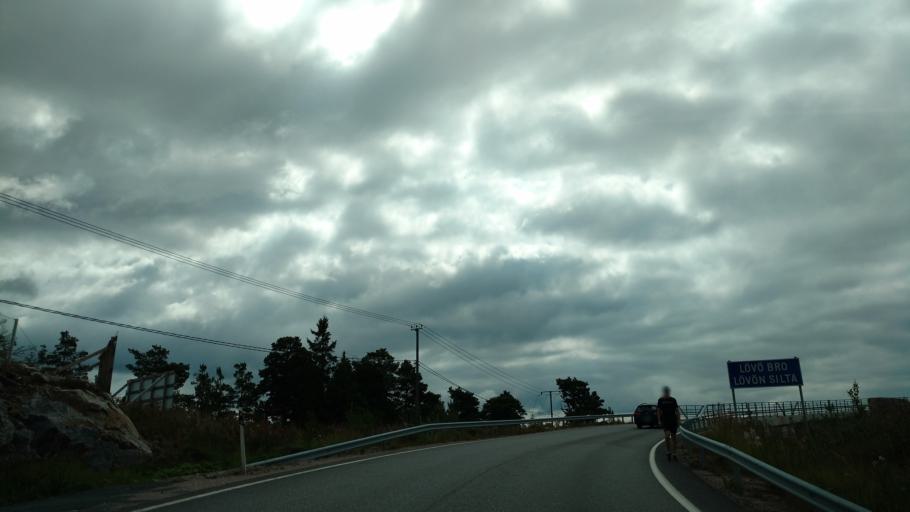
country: FI
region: Varsinais-Suomi
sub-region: Aboland-Turunmaa
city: Dragsfjaerd
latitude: 59.9871
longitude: 22.4546
